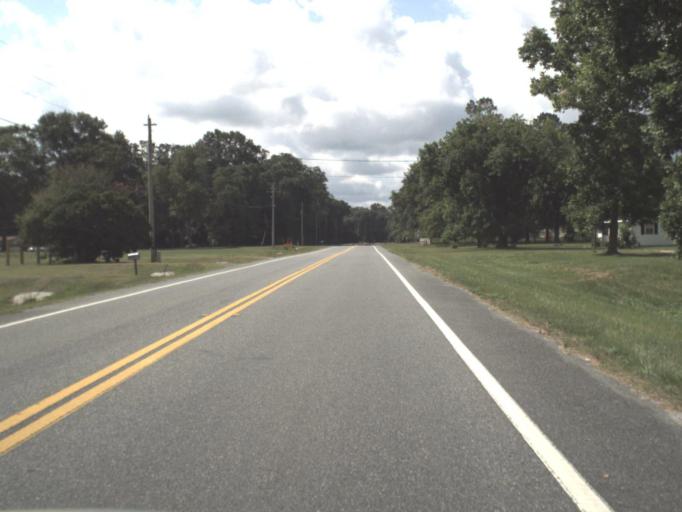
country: US
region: Florida
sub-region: Baker County
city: Macclenny
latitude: 30.3462
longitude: -82.1270
